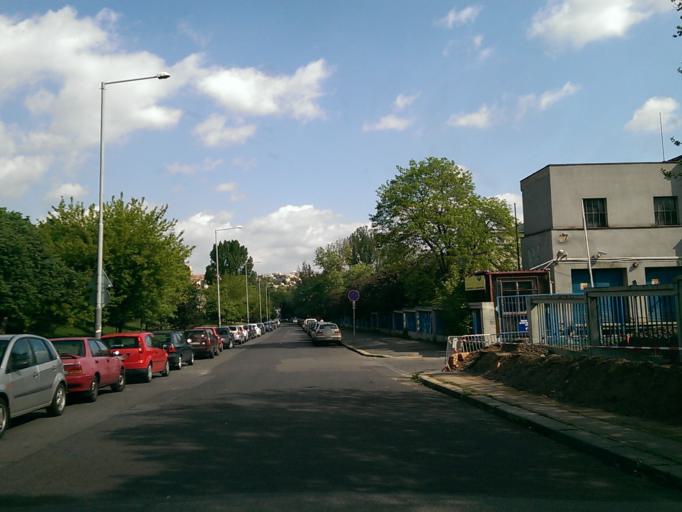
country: CZ
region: Praha
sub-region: Praha 4
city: Hodkovicky
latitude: 50.0315
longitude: 14.4560
